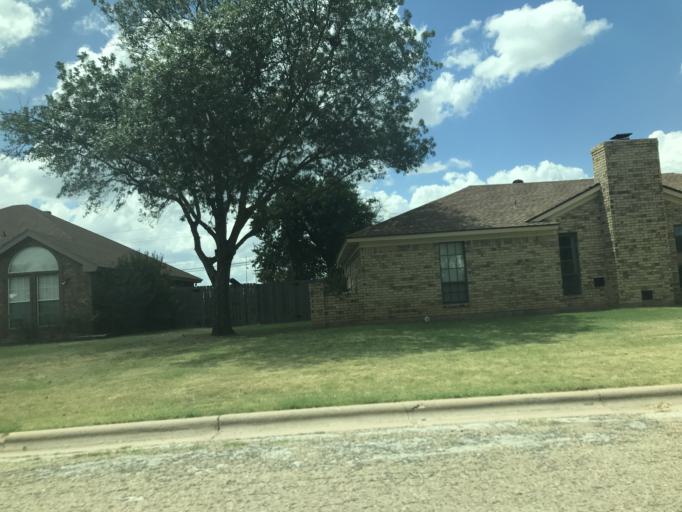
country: US
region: Texas
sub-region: Taylor County
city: Abilene
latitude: 32.4378
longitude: -99.6993
